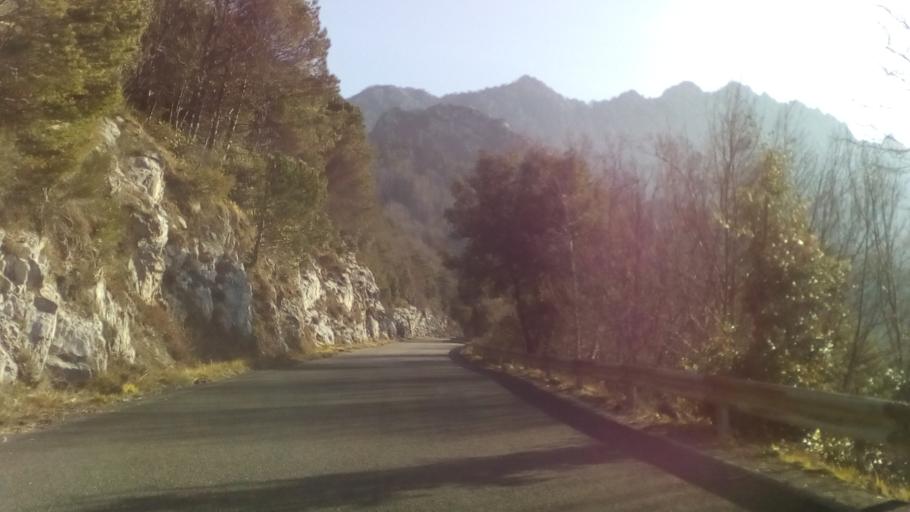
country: IT
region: Tuscany
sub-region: Provincia di Massa-Carrara
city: Montignoso
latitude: 44.0564
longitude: 10.1988
